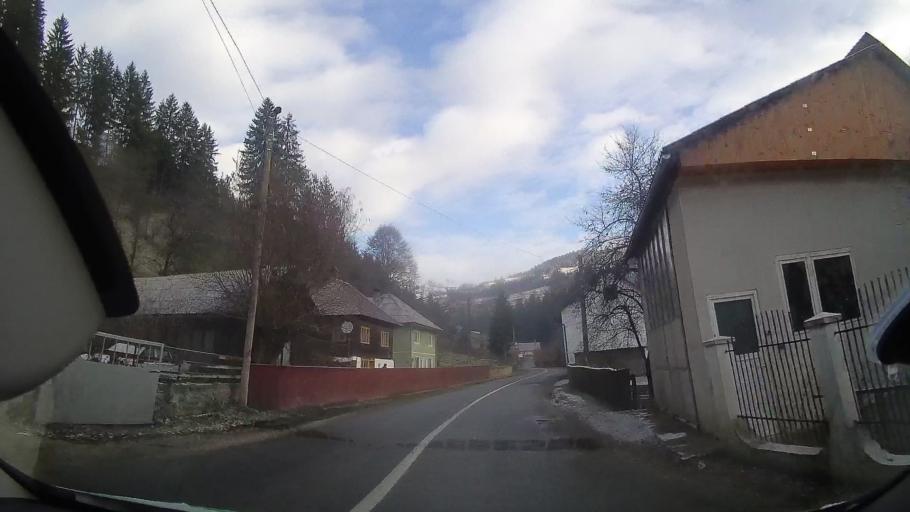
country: RO
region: Alba
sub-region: Comuna Albac
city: Albac
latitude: 46.4530
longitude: 22.9715
